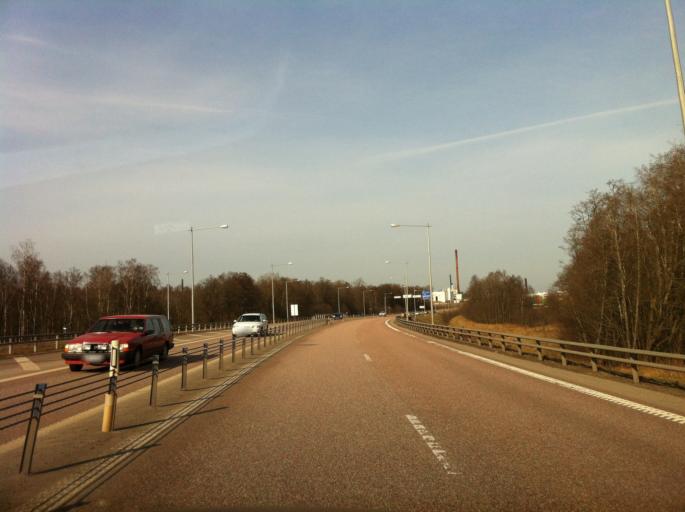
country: SE
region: Vaestra Goetaland
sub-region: Skovde Kommun
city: Skoevde
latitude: 58.3676
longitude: 13.8553
